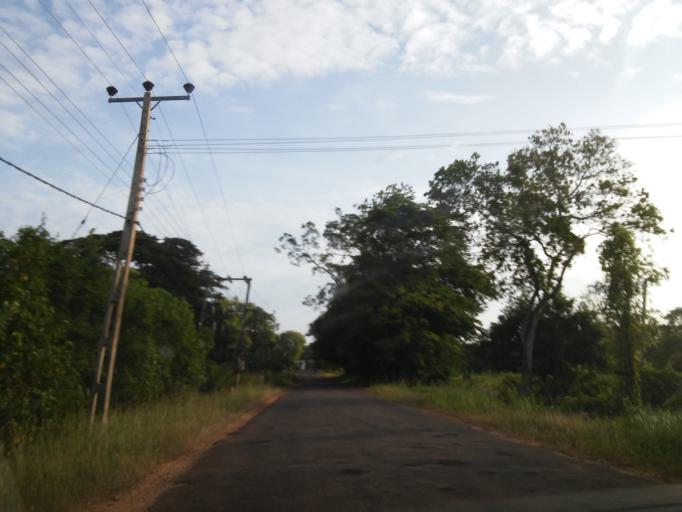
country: LK
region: Central
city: Sigiriya
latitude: 8.1320
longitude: 80.6335
